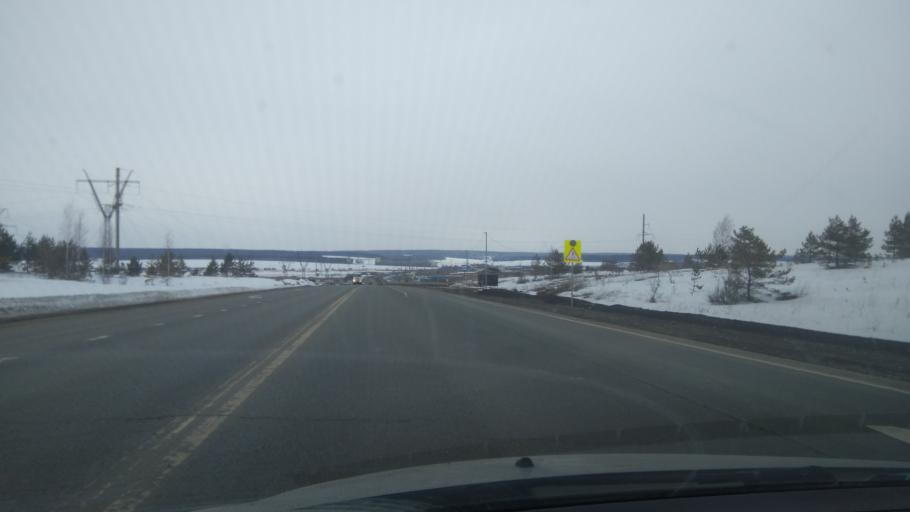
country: RU
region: Sverdlovsk
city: Achit
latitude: 56.7818
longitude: 57.9166
